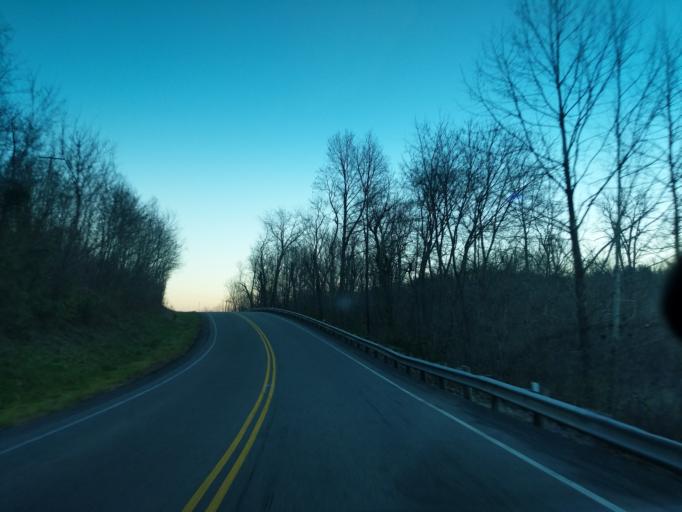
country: US
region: Ohio
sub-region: Fairfield County
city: Bremen
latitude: 39.7289
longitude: -82.4287
